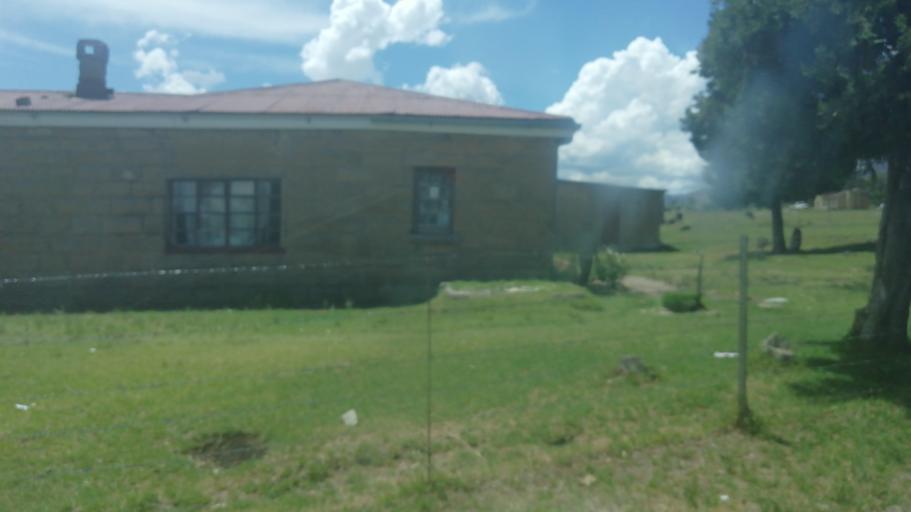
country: LS
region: Maseru
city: Nako
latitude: -29.6199
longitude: 27.5101
